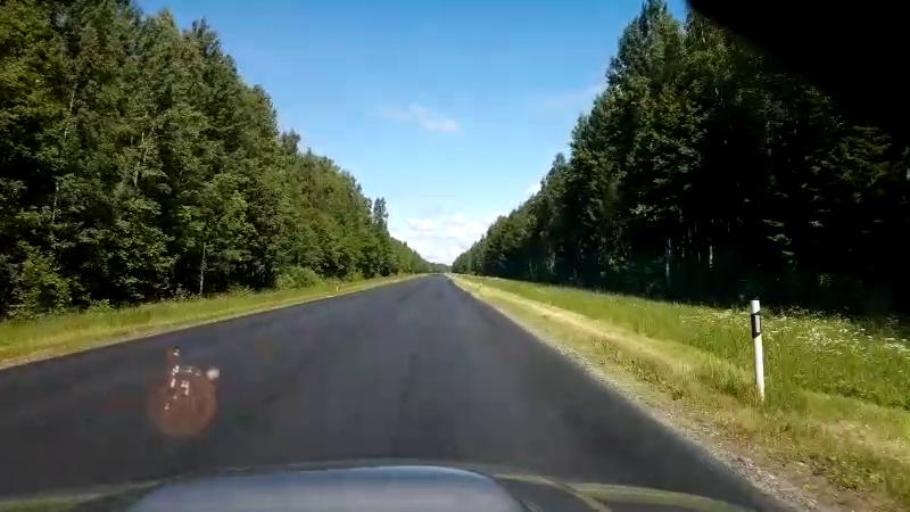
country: LV
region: Salacgrivas
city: Ainazi
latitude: 57.9571
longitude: 24.4411
